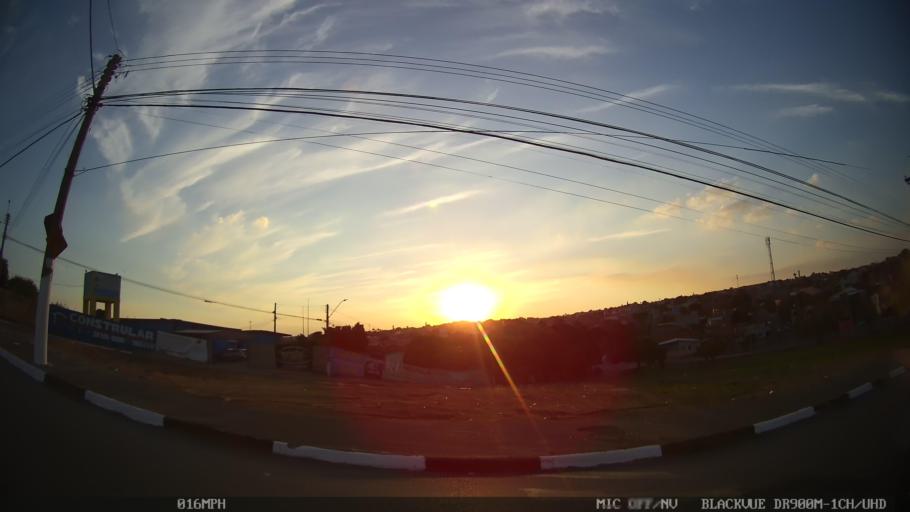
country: BR
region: Sao Paulo
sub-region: Hortolandia
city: Hortolandia
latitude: -22.8584
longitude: -47.2064
